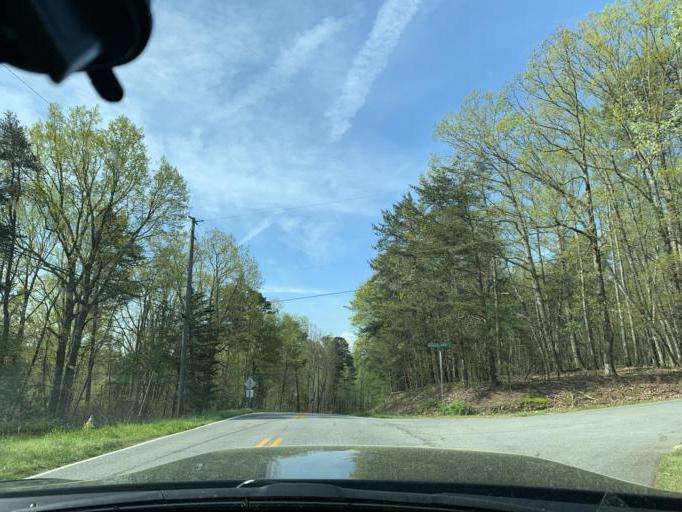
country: US
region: Georgia
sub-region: Forsyth County
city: Cumming
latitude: 34.2516
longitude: -84.1180
